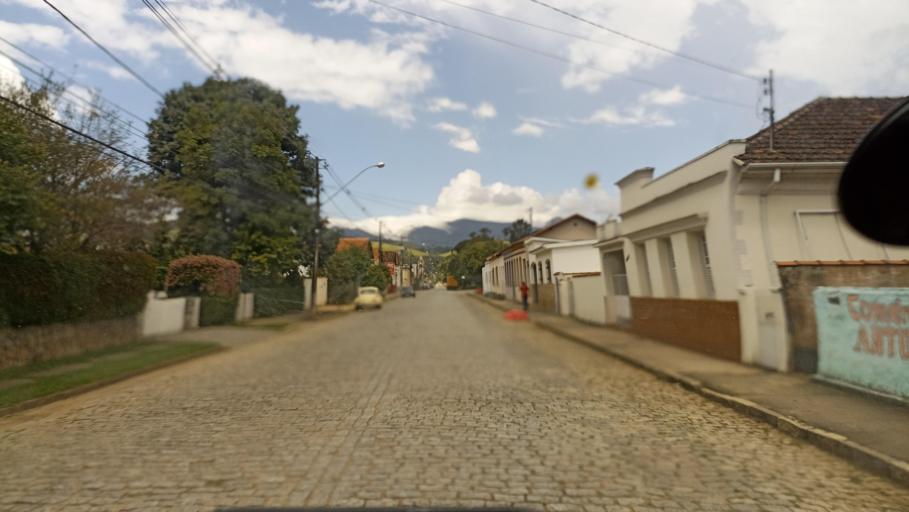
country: BR
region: Minas Gerais
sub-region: Passa Quatro
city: Passa Quatro
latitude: -22.3816
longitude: -44.9666
